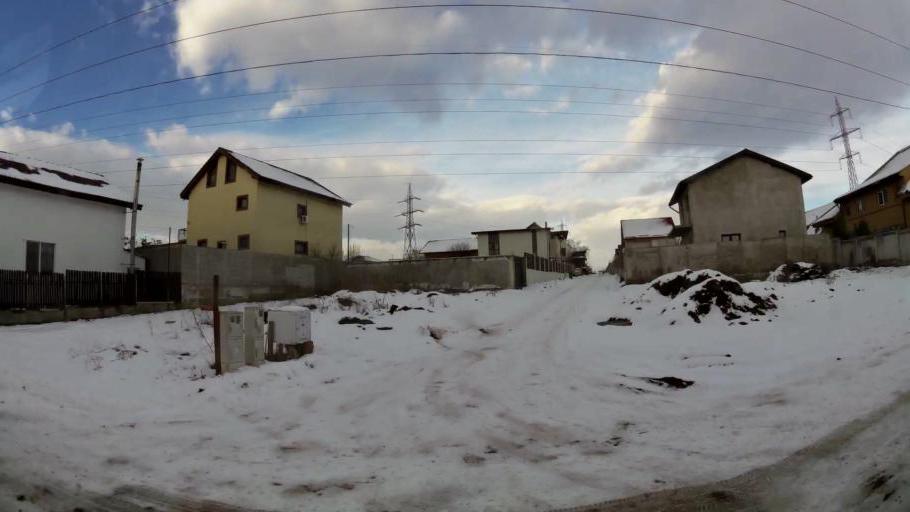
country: RO
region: Ilfov
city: Dobroesti
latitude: 44.4613
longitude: 26.1784
